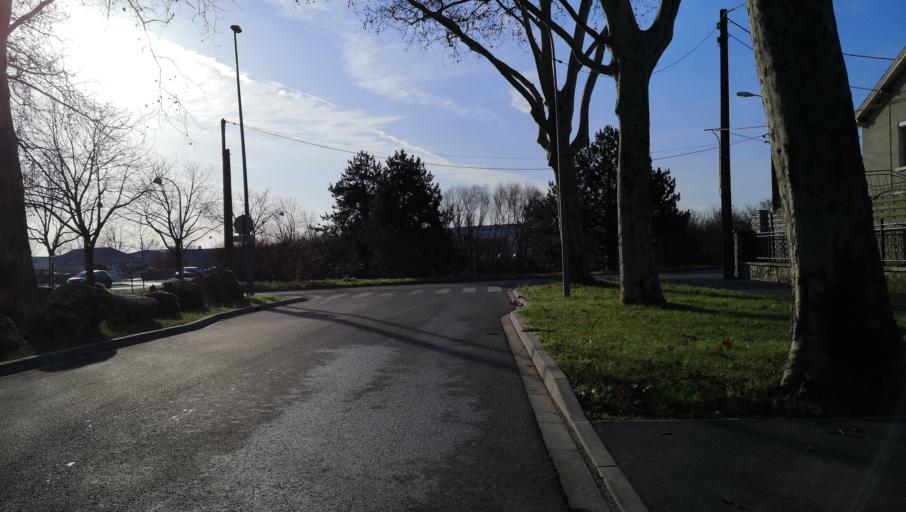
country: FR
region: Centre
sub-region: Departement du Loiret
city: Semoy
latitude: 47.9170
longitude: 1.9409
